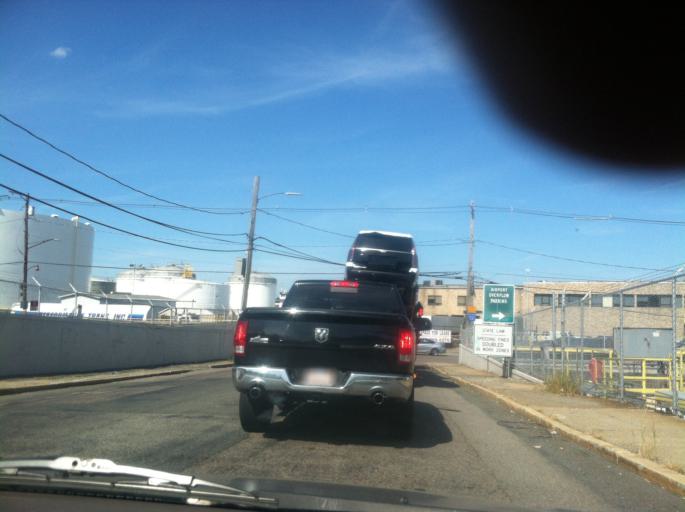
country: US
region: Massachusetts
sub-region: Suffolk County
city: Revere
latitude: 42.3907
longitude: -71.0140
